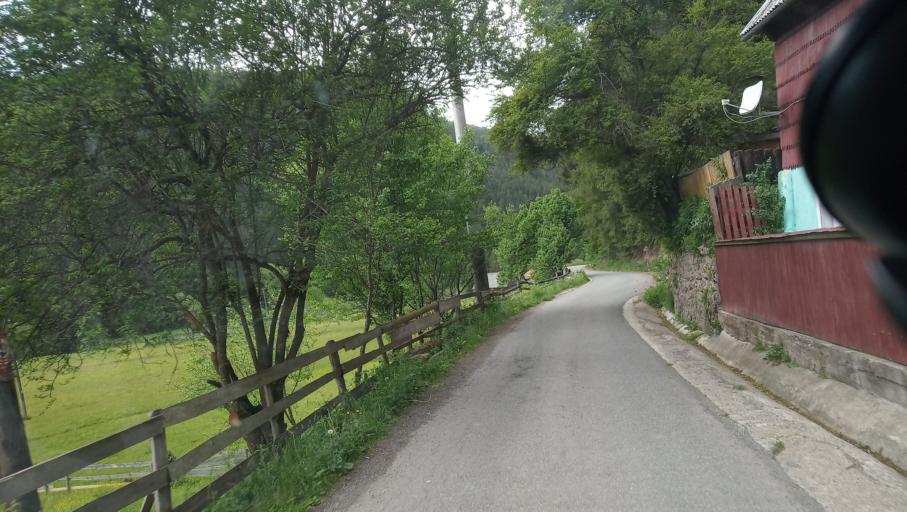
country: RO
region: Alba
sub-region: Comuna Garda de Sus
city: Garda de Sus
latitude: 46.4786
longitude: 22.8026
